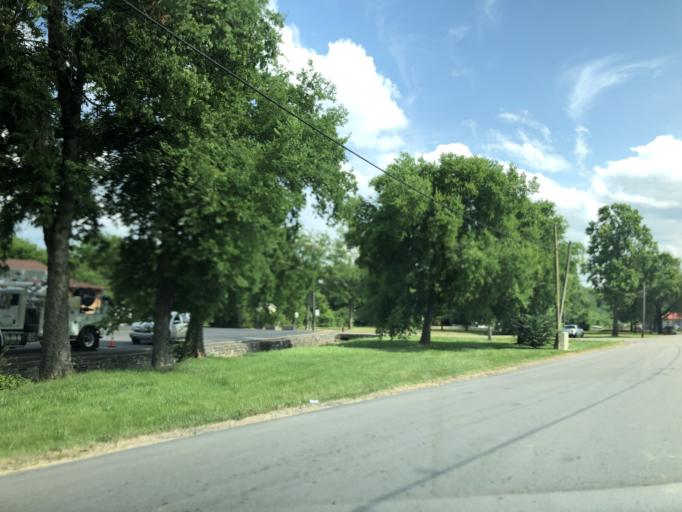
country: US
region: Tennessee
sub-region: Davidson County
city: Goodlettsville
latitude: 36.2613
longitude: -86.7105
